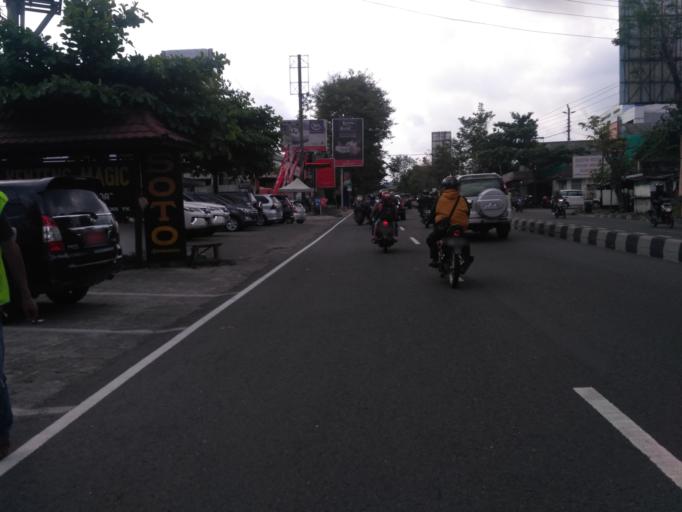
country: ID
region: Daerah Istimewa Yogyakarta
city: Melati
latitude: -7.7442
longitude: 110.3626
